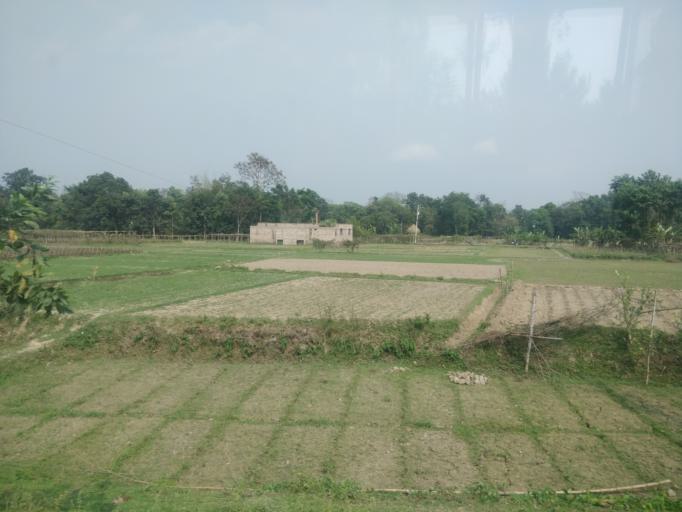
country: BD
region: Sylhet
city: Habiganj
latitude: 24.3248
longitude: 91.4332
